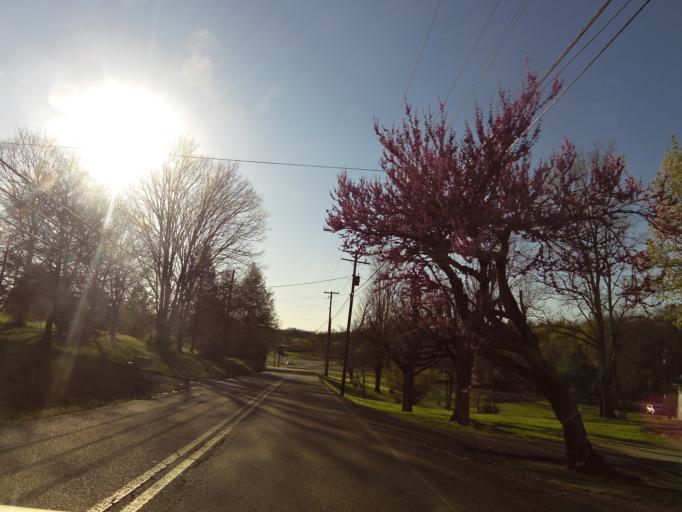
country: US
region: Tennessee
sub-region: Sevier County
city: Seymour
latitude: 35.9652
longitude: -83.7951
